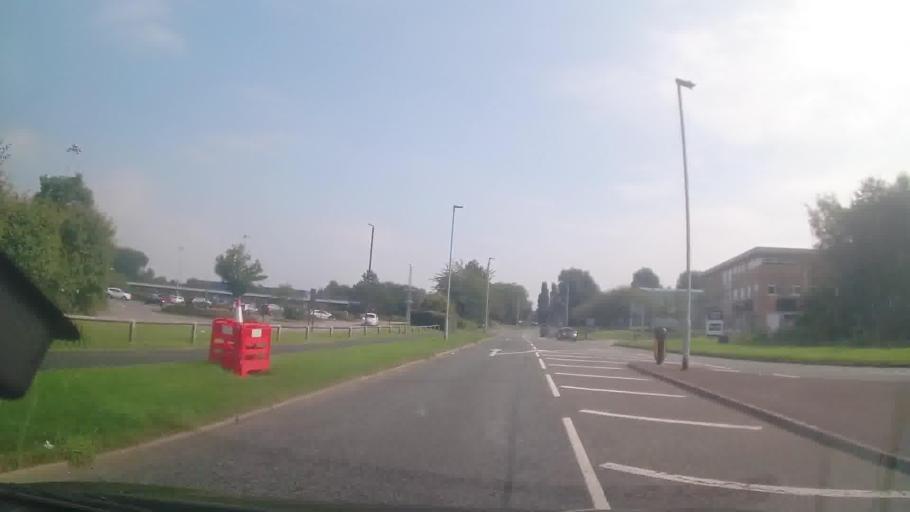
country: GB
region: England
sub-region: Warrington
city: Great Sankey
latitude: 53.4155
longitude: -2.6324
